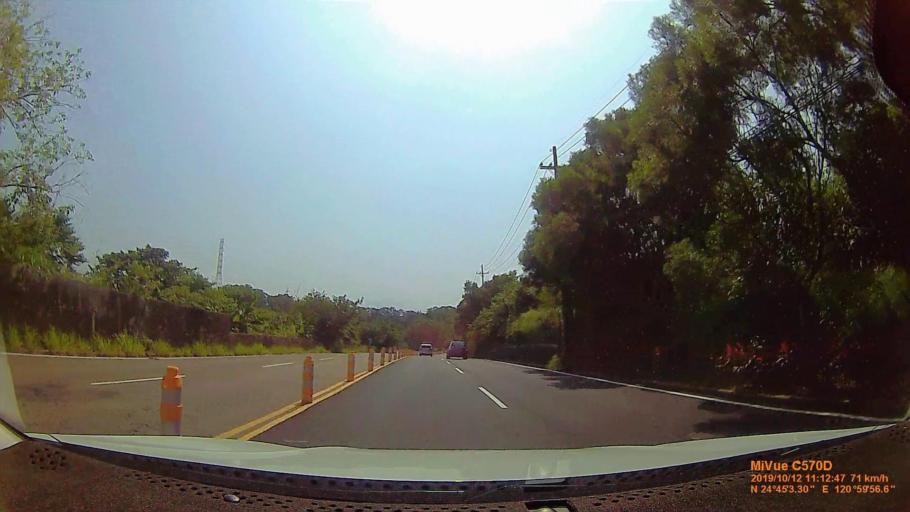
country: TW
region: Taiwan
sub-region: Hsinchu
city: Hsinchu
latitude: 24.7508
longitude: 120.9991
